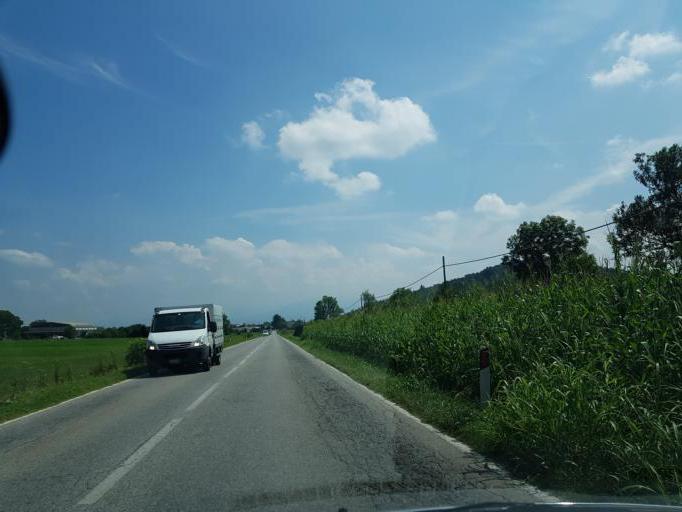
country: IT
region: Piedmont
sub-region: Provincia di Cuneo
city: Caraglio
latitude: 44.4376
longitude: 7.4155
